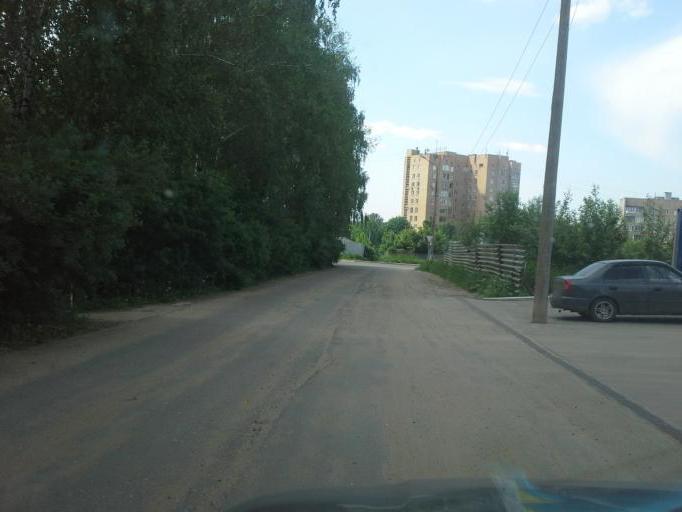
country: RU
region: Moskovskaya
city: Barvikha
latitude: 55.7228
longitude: 37.2856
